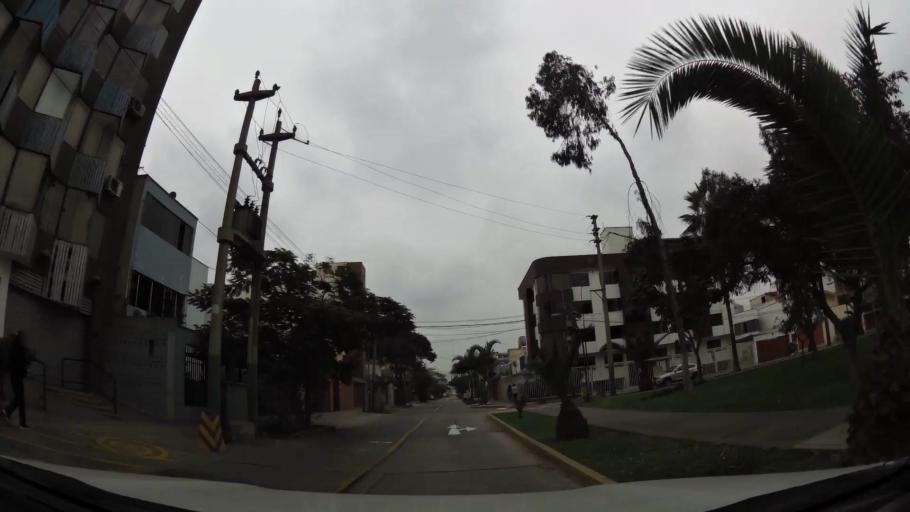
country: PE
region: Lima
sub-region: Lima
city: San Luis
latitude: -12.0925
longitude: -77.0079
